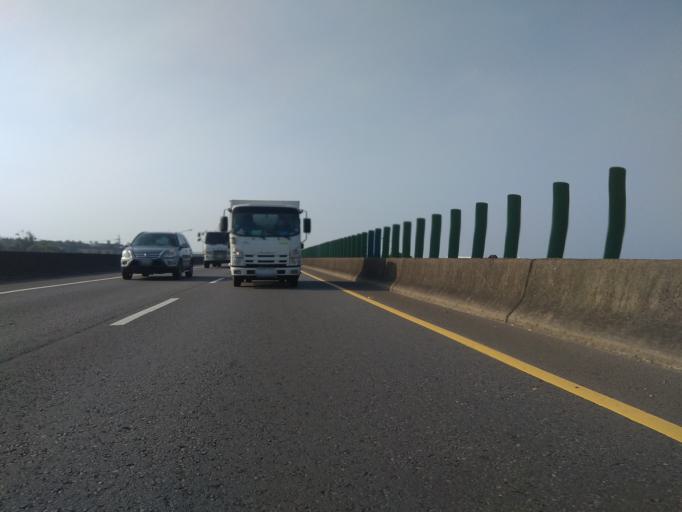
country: TW
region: Taiwan
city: Daxi
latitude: 24.9435
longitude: 121.1731
